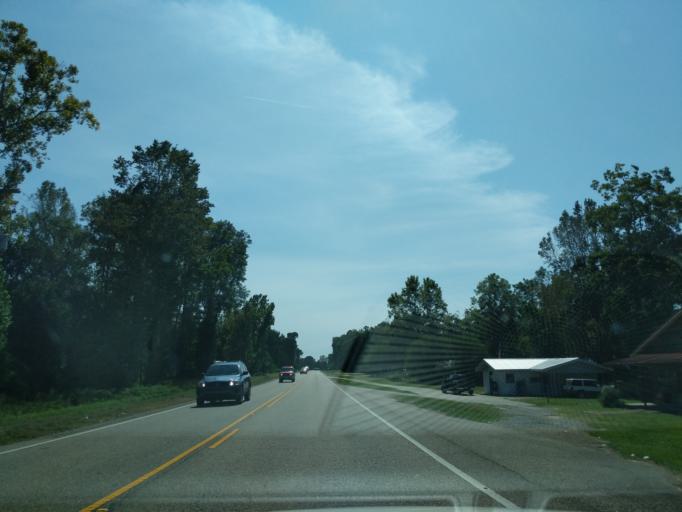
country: US
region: Florida
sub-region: Okaloosa County
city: Crestview
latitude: 31.0295
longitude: -86.6096
